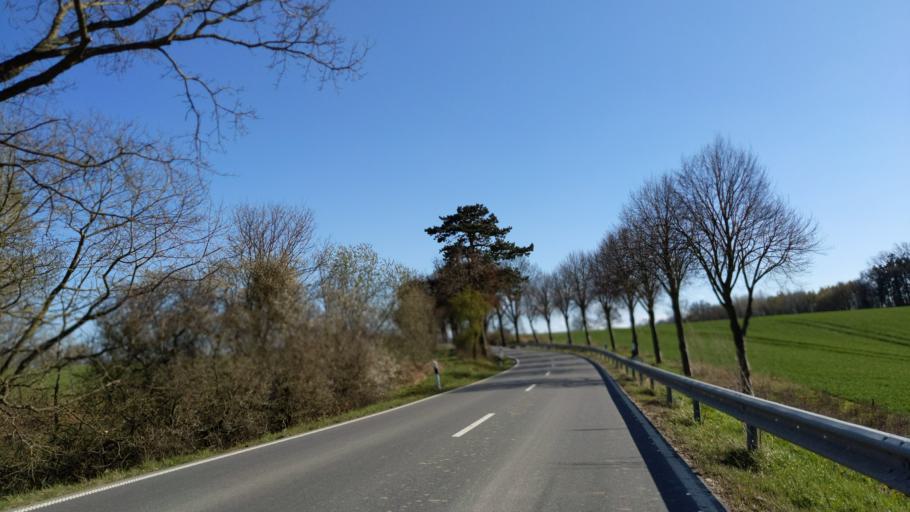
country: DE
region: Schleswig-Holstein
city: Eutin
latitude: 54.0847
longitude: 10.6196
